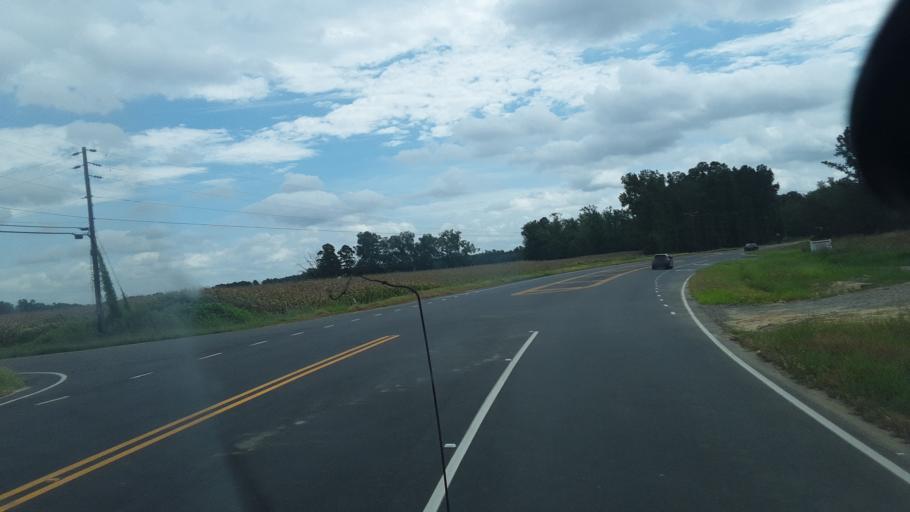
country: US
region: North Carolina
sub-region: Robeson County
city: Rowland
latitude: 34.5320
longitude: -79.2812
